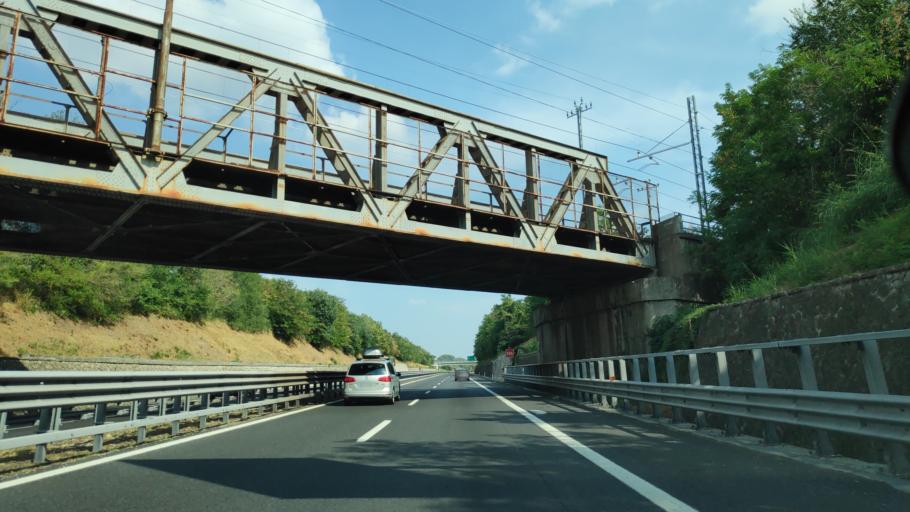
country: IT
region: Umbria
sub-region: Provincia di Terni
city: Attigliano
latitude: 42.5039
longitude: 12.3044
